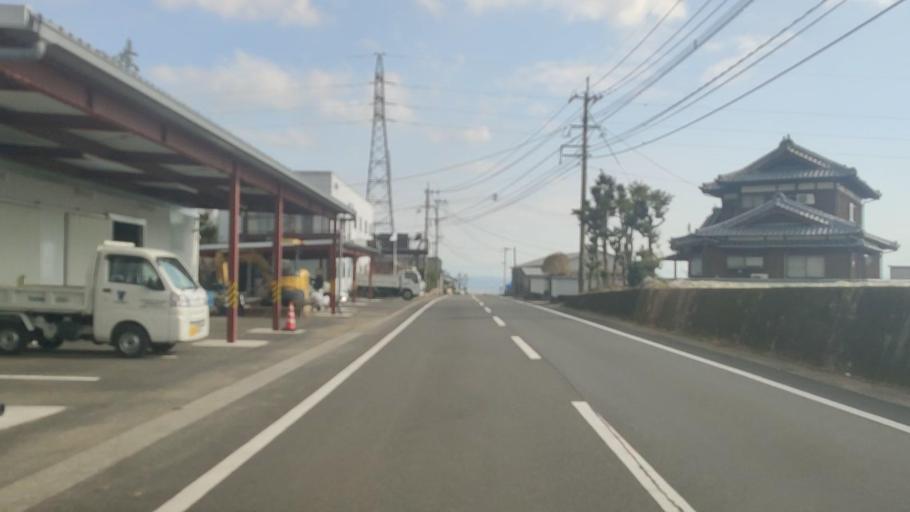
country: JP
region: Nagasaki
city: Shimabara
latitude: 32.6701
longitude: 130.2843
